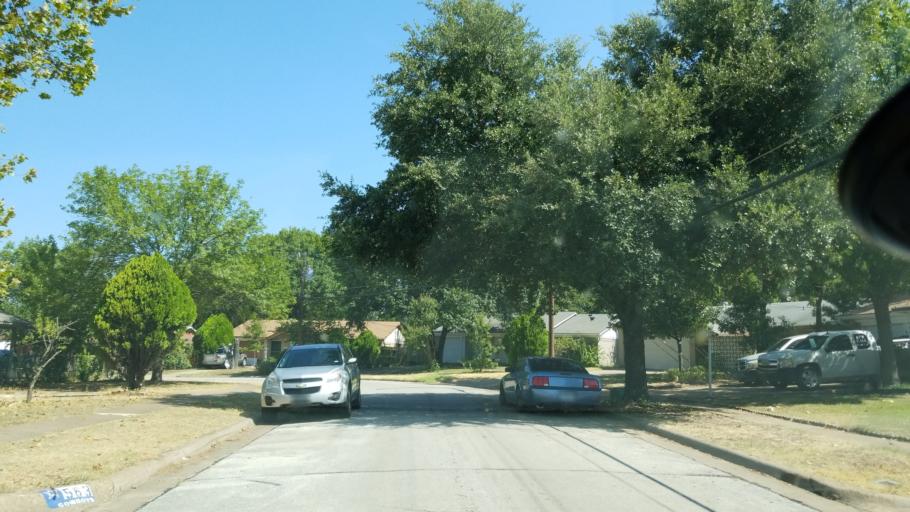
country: US
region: Texas
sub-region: Dallas County
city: Duncanville
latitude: 32.6588
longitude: -96.9005
